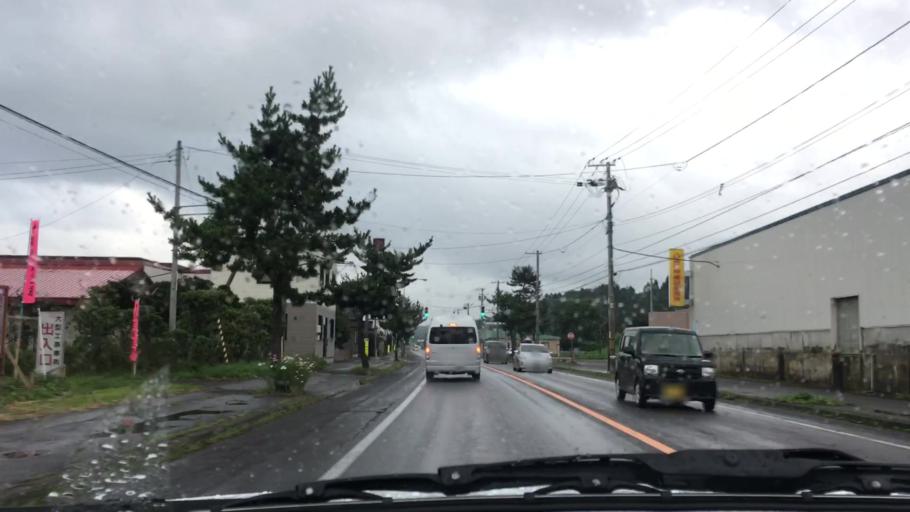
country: JP
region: Hokkaido
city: Nanae
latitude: 42.2320
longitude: 140.3258
